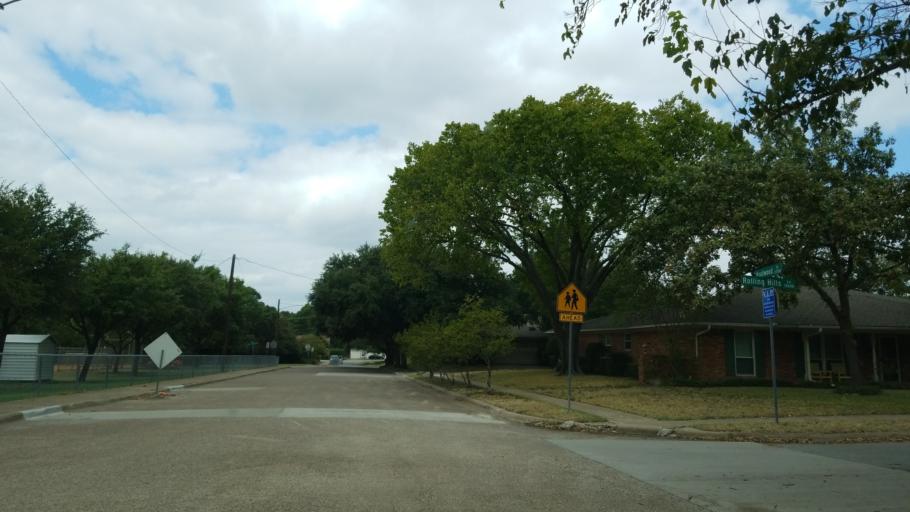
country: US
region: Texas
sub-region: Dallas County
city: Richardson
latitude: 32.9342
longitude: -96.7752
